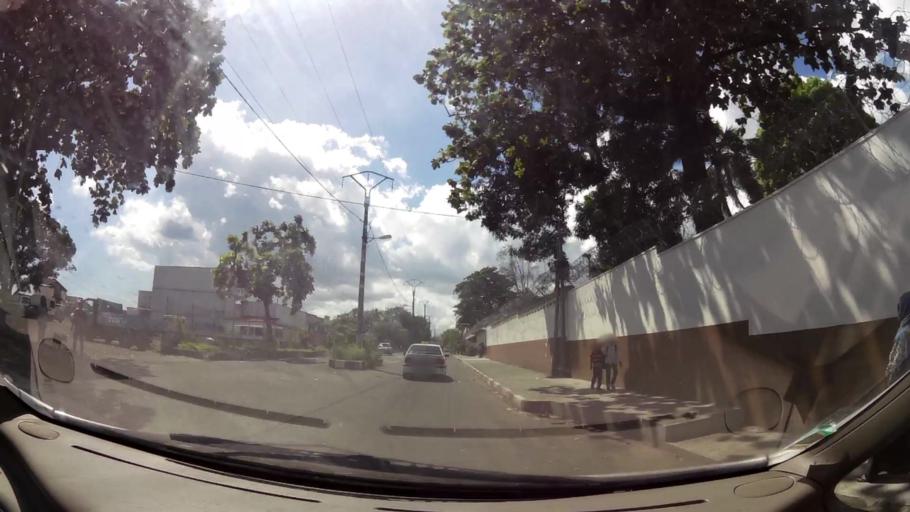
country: KM
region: Grande Comore
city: Mavingouni
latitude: -11.7101
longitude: 43.2466
